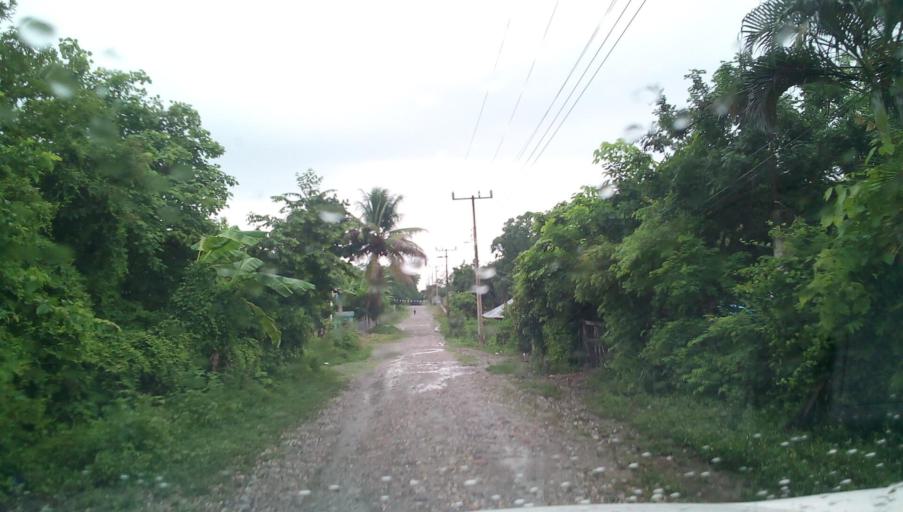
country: MX
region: Veracruz
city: Tempoal de Sanchez
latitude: 21.4166
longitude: -98.4266
